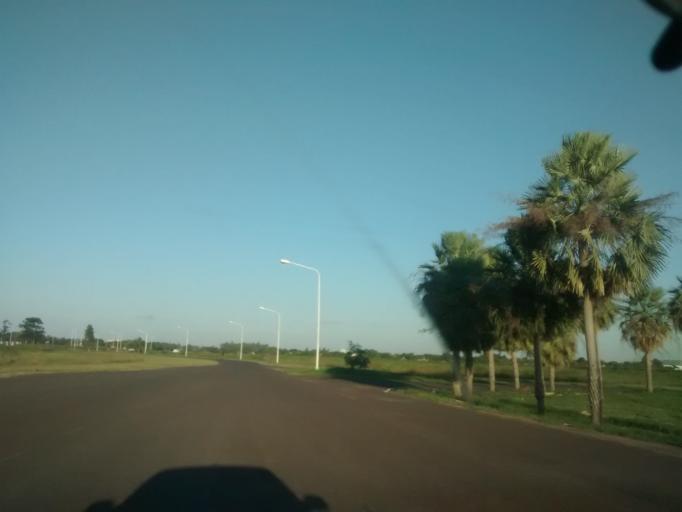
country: AR
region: Chaco
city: Fontana
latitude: -27.4448
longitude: -59.0475
